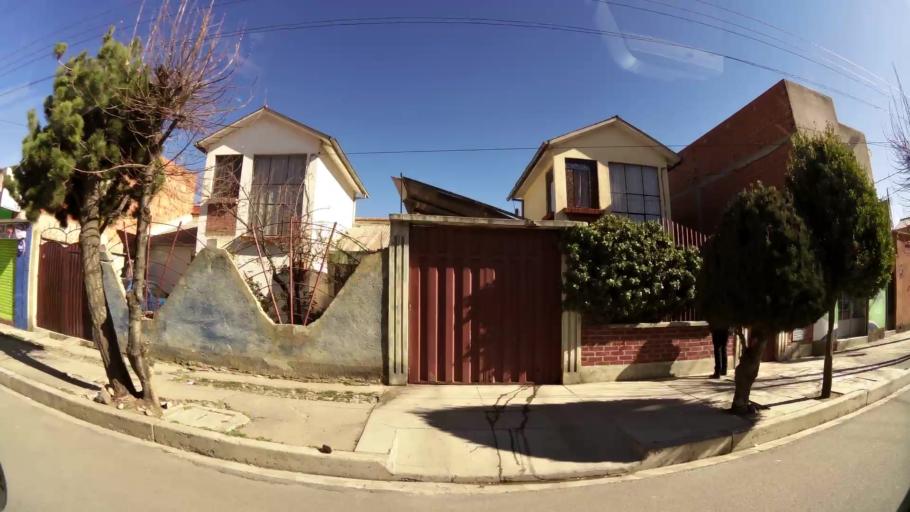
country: BO
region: La Paz
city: La Paz
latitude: -16.5265
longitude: -68.2094
